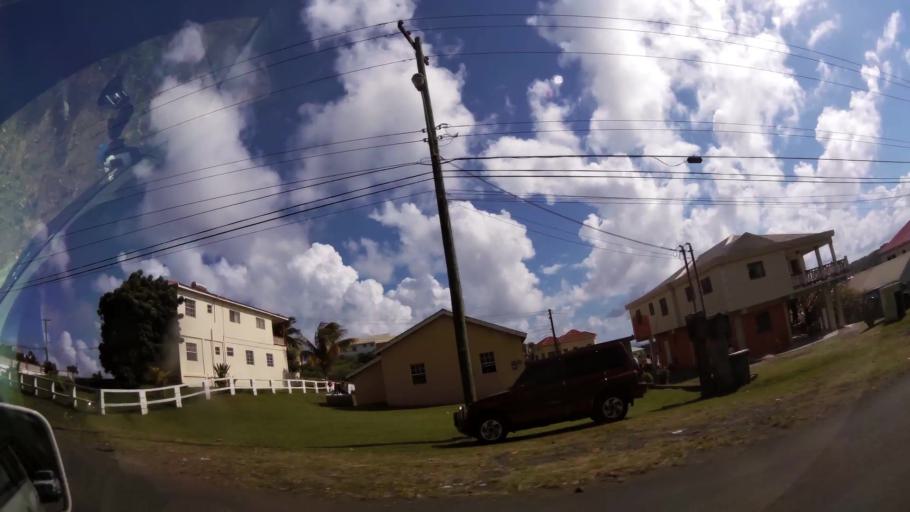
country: VC
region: Saint George
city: Kingstown
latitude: 13.1437
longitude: -61.1677
